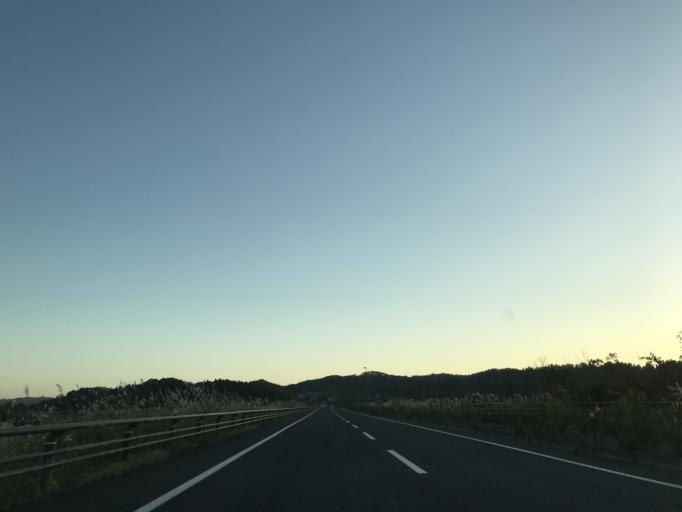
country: JP
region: Iwate
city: Ichinoseki
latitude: 39.0077
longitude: 141.1160
